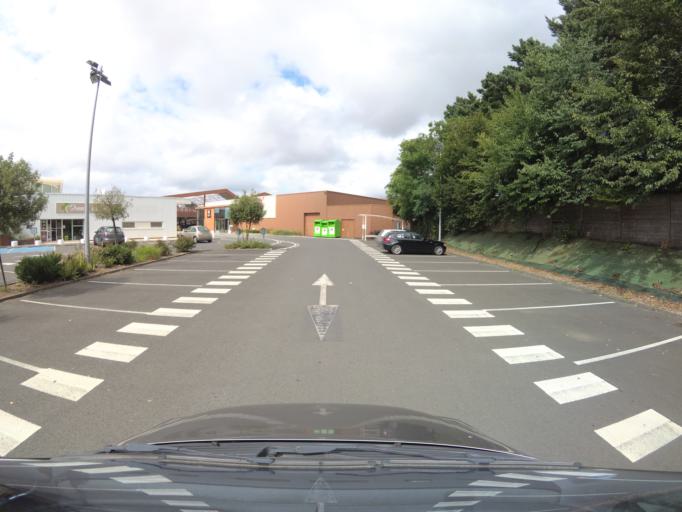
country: FR
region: Pays de la Loire
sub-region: Departement de la Loire-Atlantique
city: Saint-Philbert-de-Grand-Lieu
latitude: 47.0457
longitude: -1.6422
